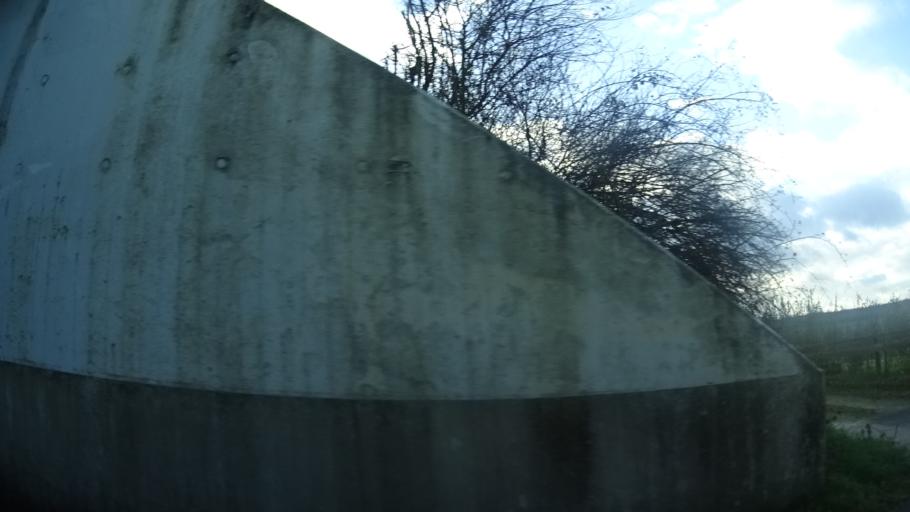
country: DE
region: Hesse
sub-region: Regierungsbezirk Kassel
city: Hunfeld
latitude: 50.6414
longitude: 9.7491
